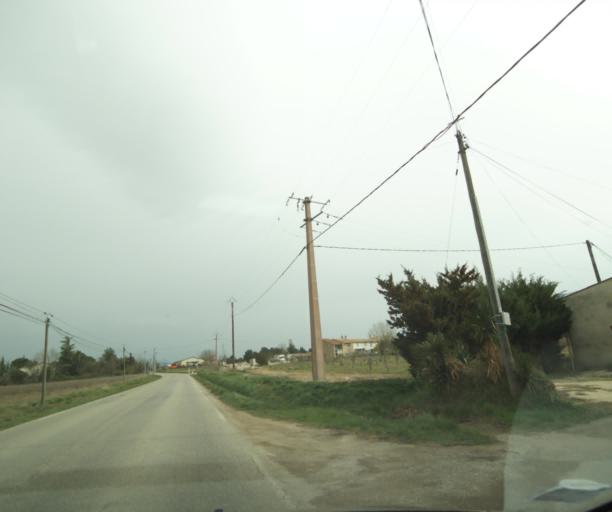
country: FR
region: Provence-Alpes-Cote d'Azur
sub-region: Departement des Bouches-du-Rhone
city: Trets
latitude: 43.4540
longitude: 5.6941
